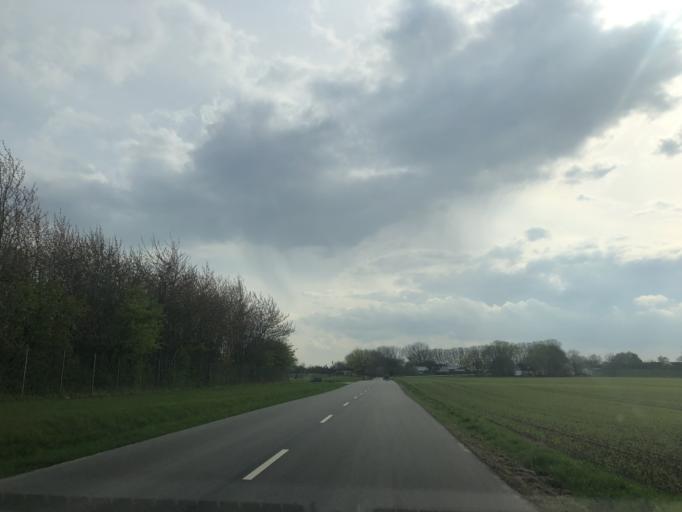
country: DK
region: Zealand
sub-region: Roskilde Kommune
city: Gundsomagle
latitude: 55.7051
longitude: 12.1525
